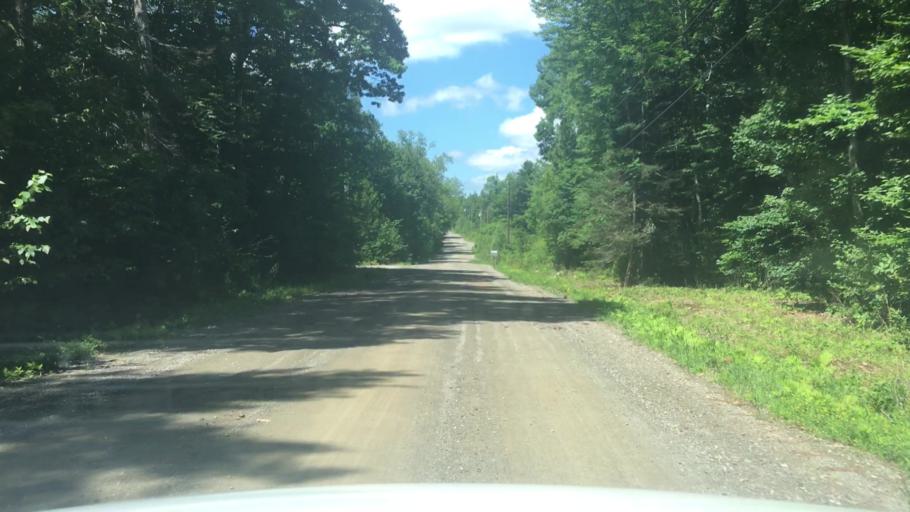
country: US
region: Maine
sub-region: Waldo County
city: Northport
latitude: 44.3456
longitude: -68.9626
